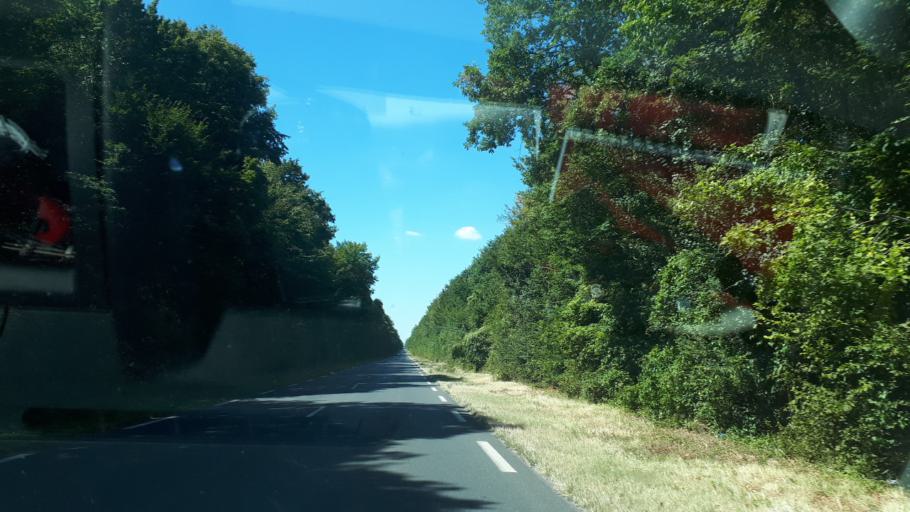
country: FR
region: Centre
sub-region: Departement du Loir-et-Cher
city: Mont-pres-Chambord
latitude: 47.5623
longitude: 1.4219
